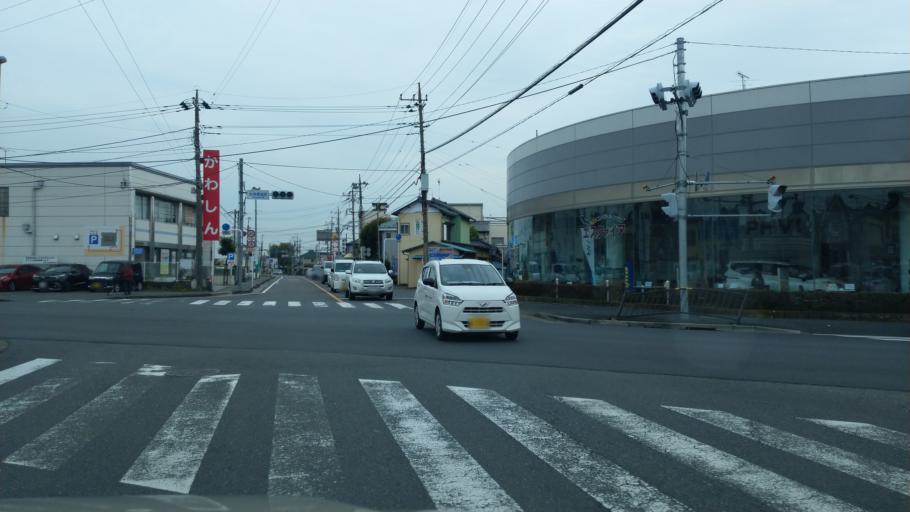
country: JP
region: Saitama
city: Iwatsuki
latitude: 35.9431
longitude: 139.7080
